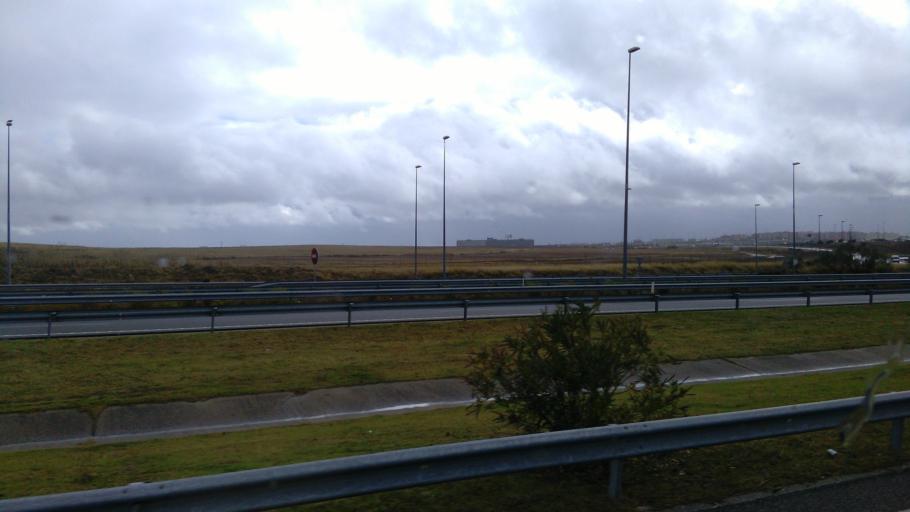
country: ES
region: Madrid
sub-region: Provincia de Madrid
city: Alcorcon
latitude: 40.3220
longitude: -3.8191
